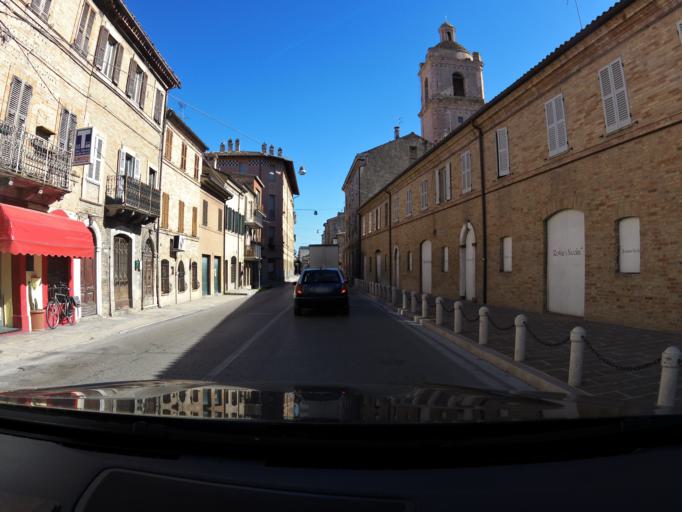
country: IT
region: The Marches
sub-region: Province of Fermo
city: Porto San Giorgio
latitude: 43.1812
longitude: 13.7928
